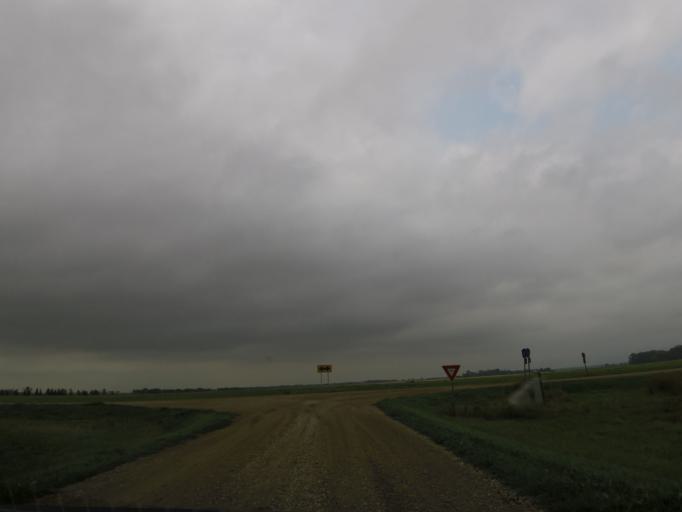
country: US
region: North Dakota
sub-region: Walsh County
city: Grafton
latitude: 48.4701
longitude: -97.1758
